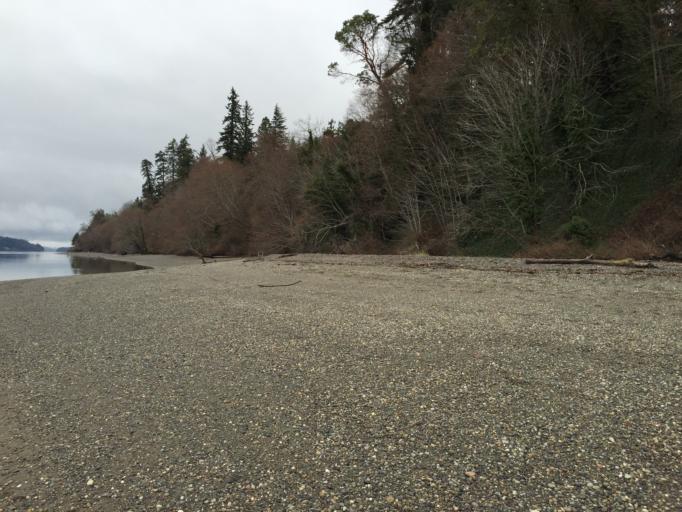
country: US
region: Washington
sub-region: Thurston County
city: Olympia
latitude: 47.1327
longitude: -122.9059
